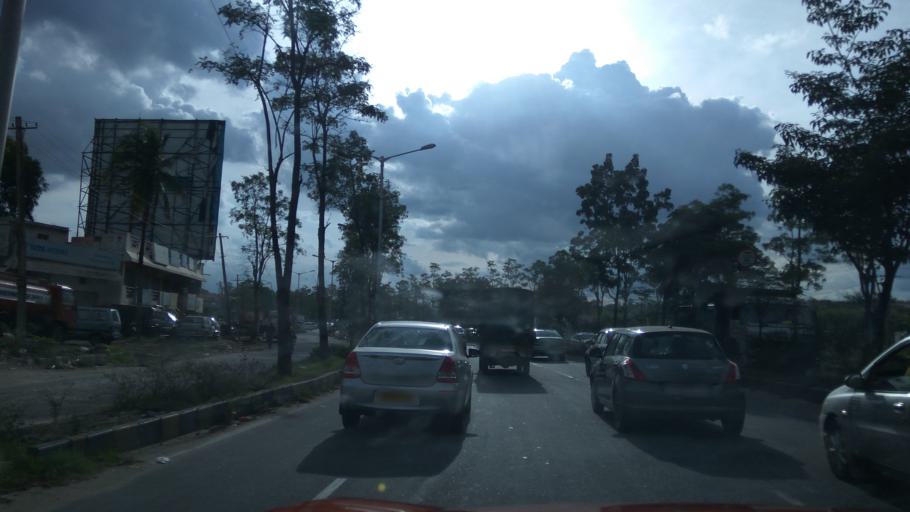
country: IN
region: Karnataka
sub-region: Bangalore Urban
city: Yelahanka
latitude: 13.0436
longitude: 77.5997
